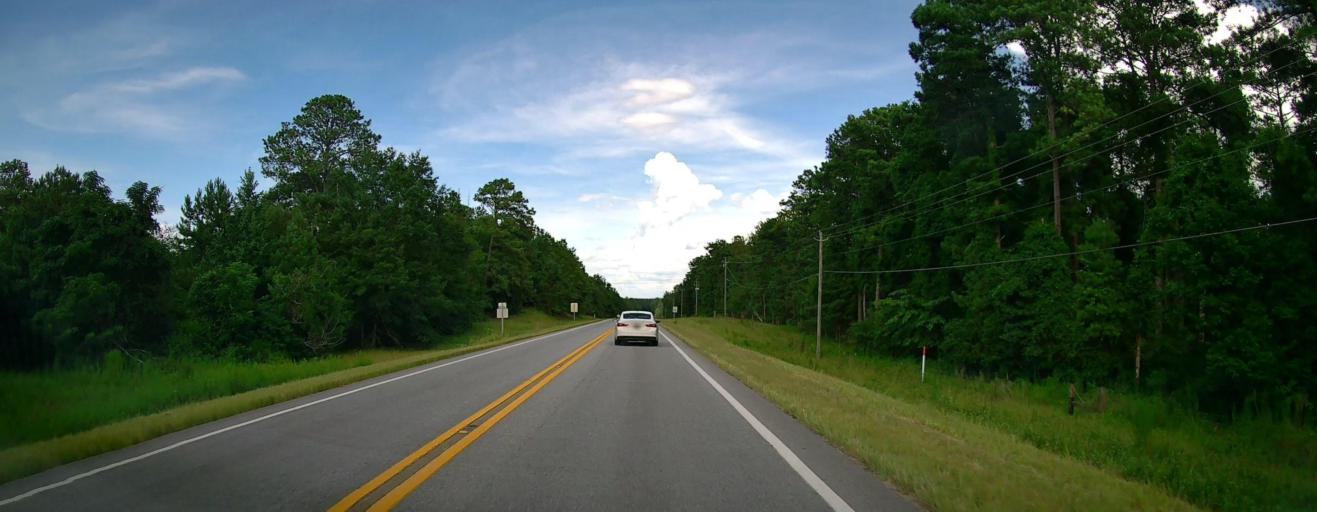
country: US
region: Alabama
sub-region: Russell County
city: Ladonia
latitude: 32.4577
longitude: -85.1835
